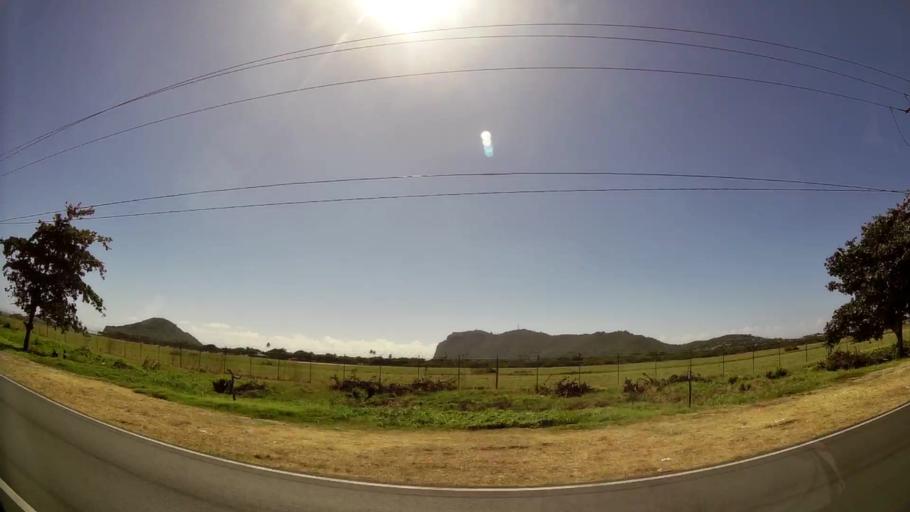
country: LC
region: Vieux-Fort
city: Vieux Fort
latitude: 13.7356
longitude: -60.9424
